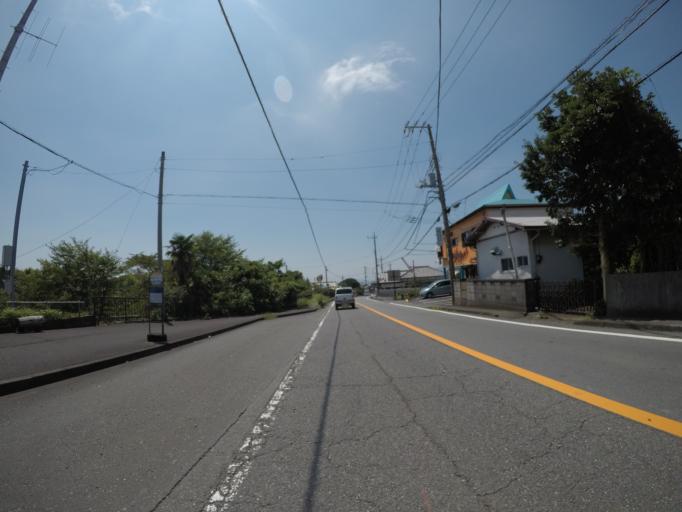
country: JP
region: Shizuoka
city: Fuji
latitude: 35.2001
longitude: 138.6832
